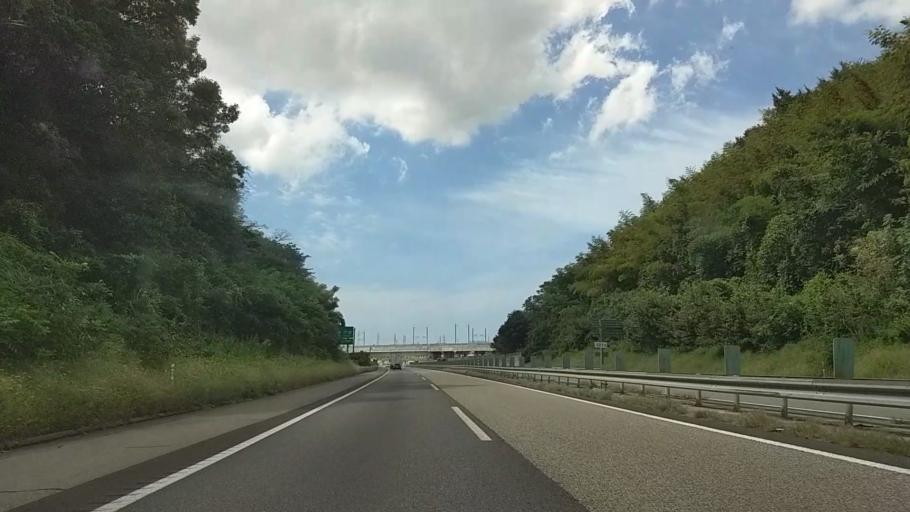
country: JP
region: Ishikawa
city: Kanazawa-shi
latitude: 36.6090
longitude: 136.6910
